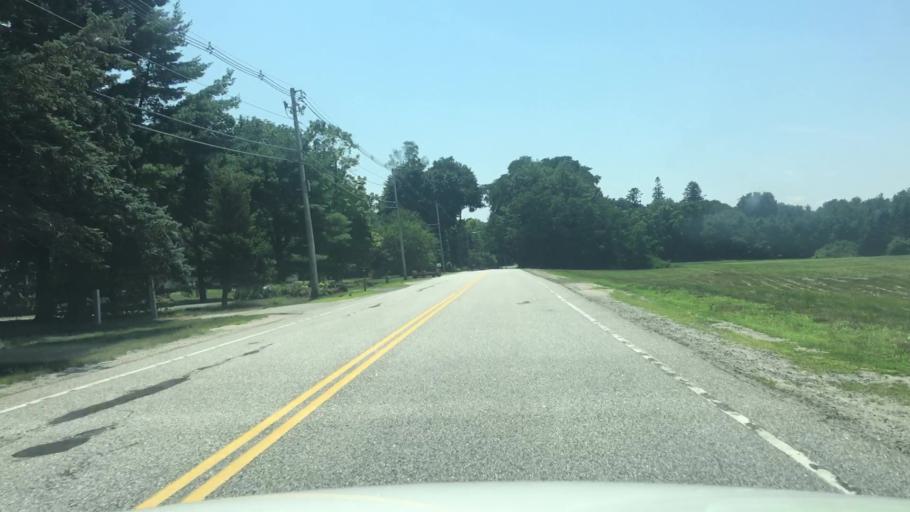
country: US
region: Maine
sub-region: Cumberland County
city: Cumberland Center
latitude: 43.7693
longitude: -70.2702
